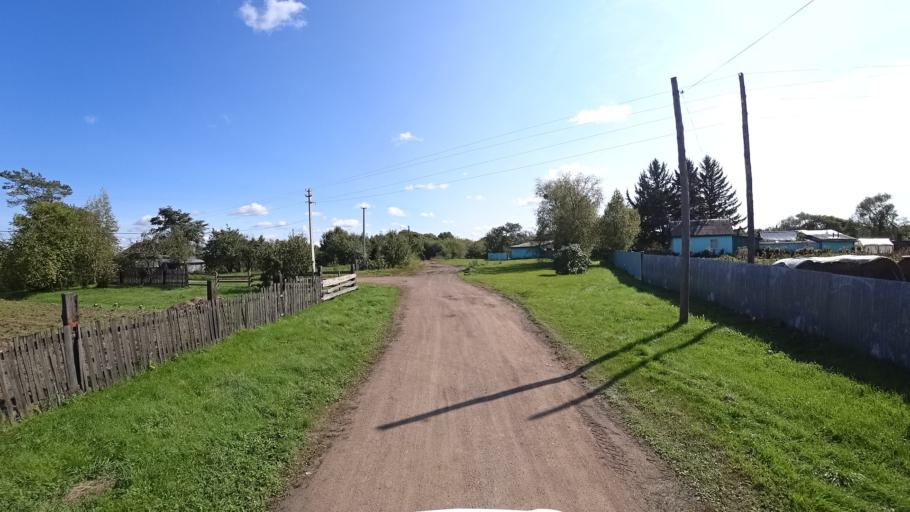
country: RU
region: Amur
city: Arkhara
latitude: 49.4015
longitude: 130.1536
